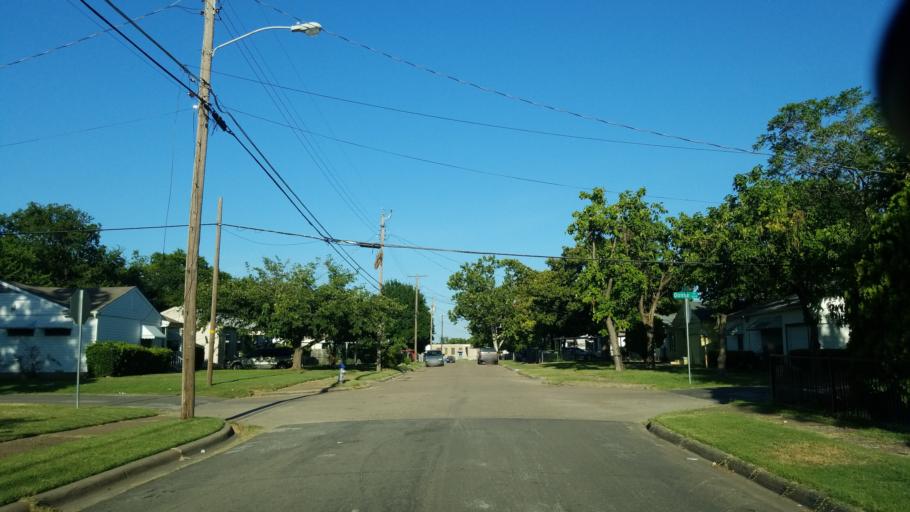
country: US
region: Texas
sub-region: Dallas County
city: Balch Springs
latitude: 32.7747
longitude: -96.7050
